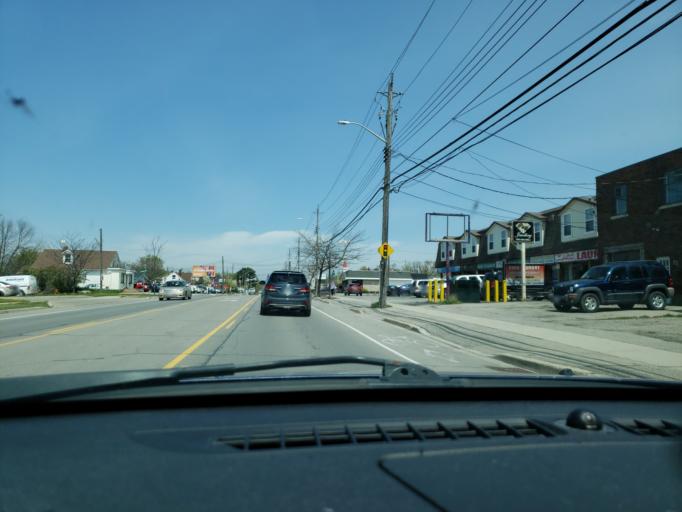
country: CA
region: Ontario
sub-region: Regional Municipality of Niagara
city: St. Catharines
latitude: 43.1535
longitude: -79.2144
